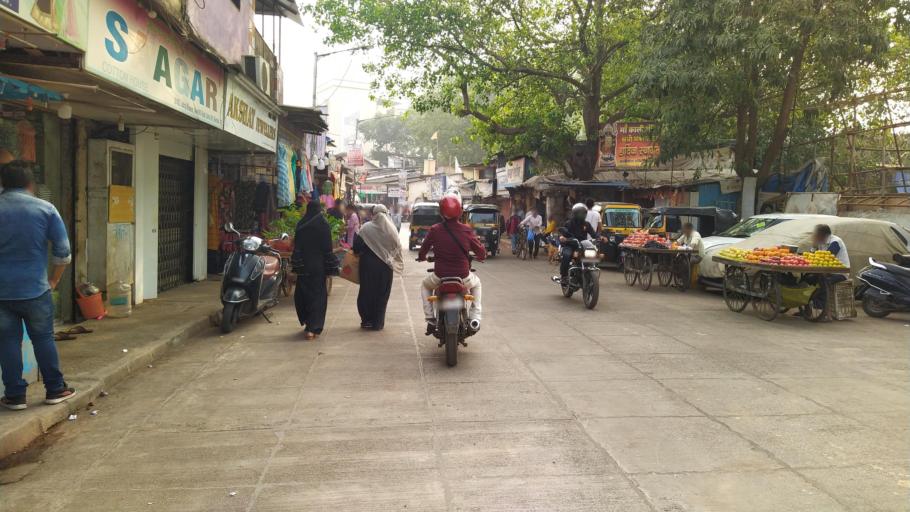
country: IN
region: Maharashtra
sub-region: Mumbai Suburban
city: Mumbai
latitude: 19.0709
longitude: 72.8779
